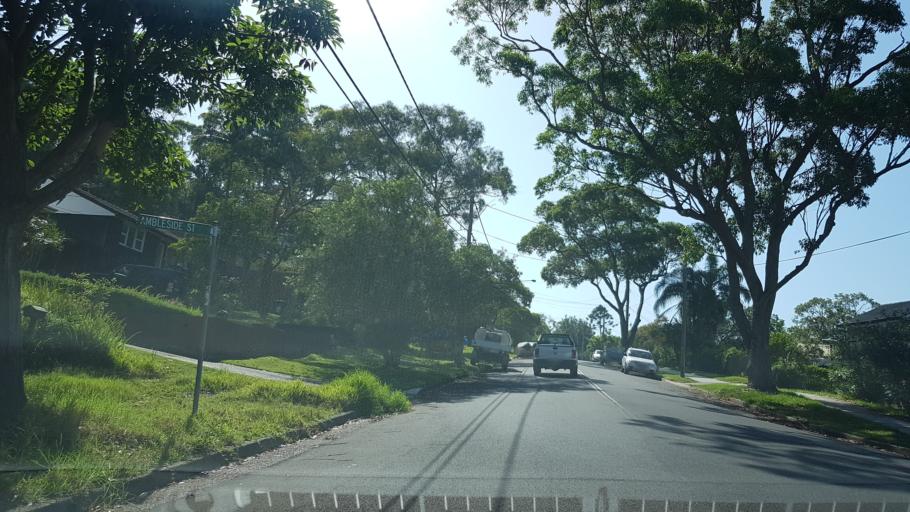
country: AU
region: New South Wales
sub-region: Warringah
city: Narrabeen
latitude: -33.7301
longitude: 151.2804
